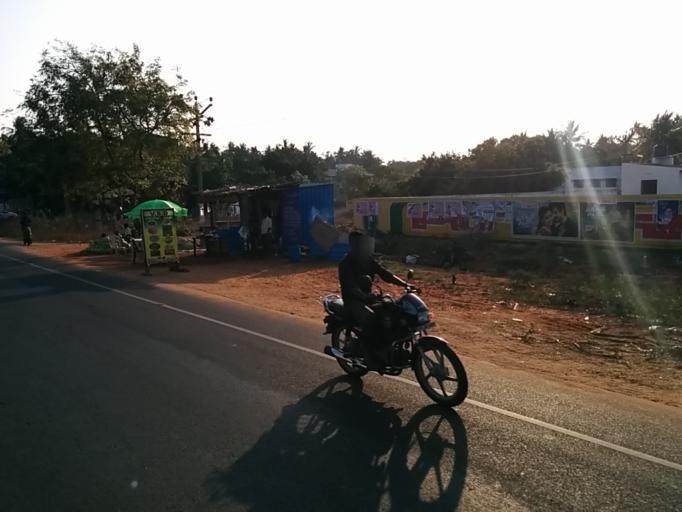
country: IN
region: Tamil Nadu
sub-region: Villupuram
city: Auroville
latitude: 12.0044
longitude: 79.8544
